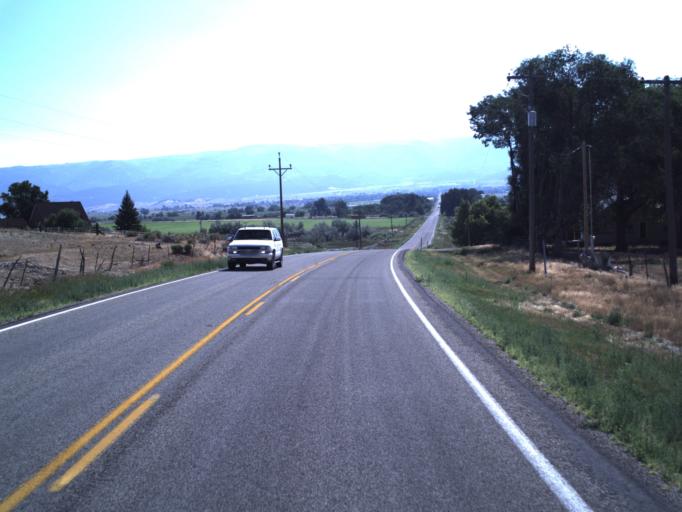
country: US
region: Utah
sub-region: Sanpete County
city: Mount Pleasant
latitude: 39.5467
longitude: -111.5241
